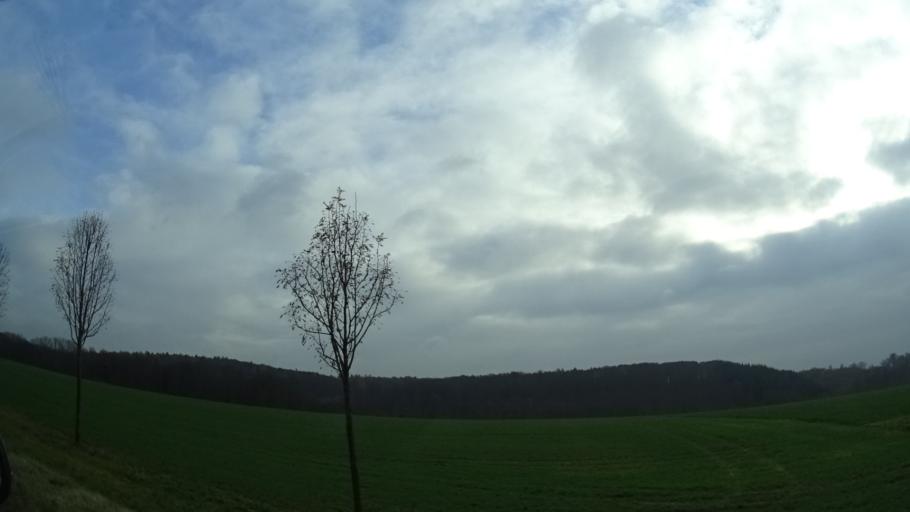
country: DE
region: Baden-Wuerttemberg
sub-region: Karlsruhe Region
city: Spechbach
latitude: 49.3668
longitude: 8.8747
